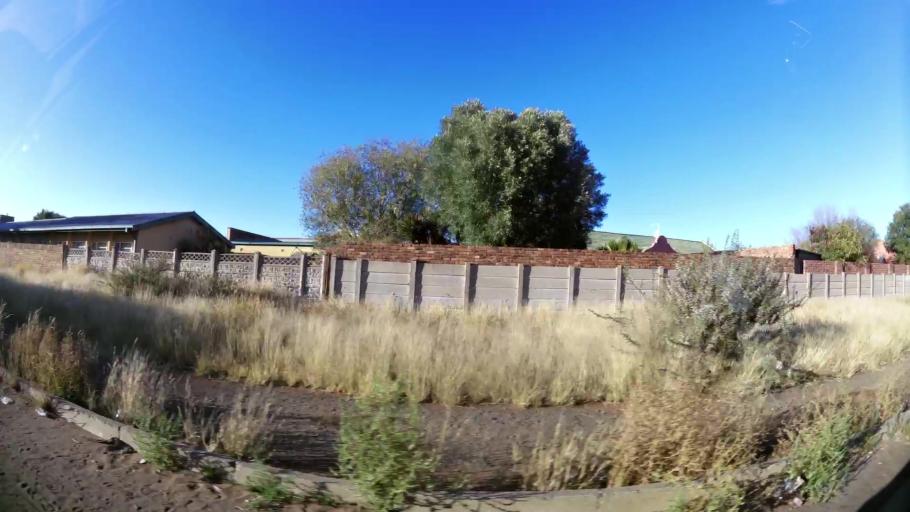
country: ZA
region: Northern Cape
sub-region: Frances Baard District Municipality
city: Kimberley
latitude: -28.7502
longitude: 24.7510
